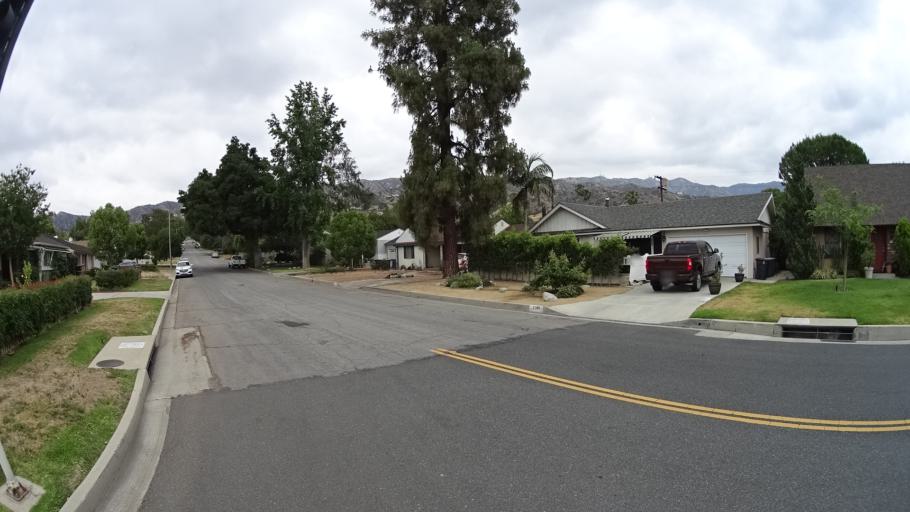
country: US
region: California
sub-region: Los Angeles County
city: Burbank
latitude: 34.2003
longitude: -118.3295
